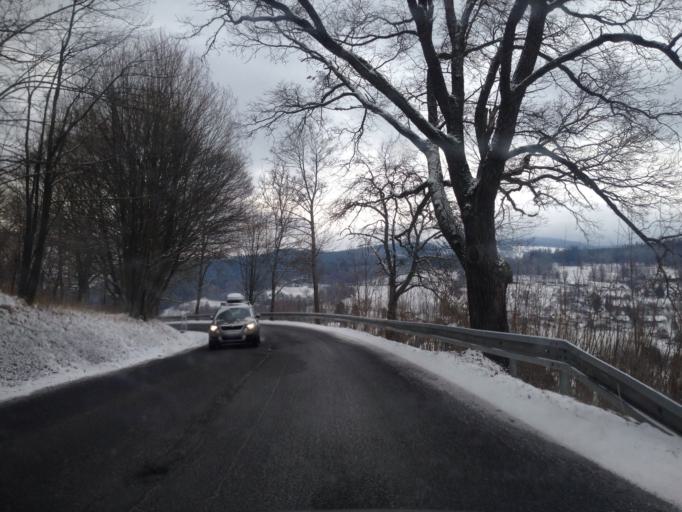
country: CZ
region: Liberecky
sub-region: Okres Semily
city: Vysoke nad Jizerou
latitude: 50.6979
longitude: 15.3885
